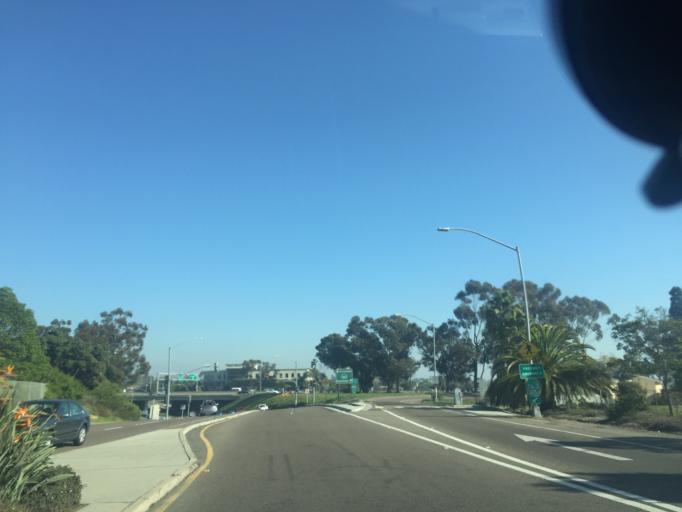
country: US
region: California
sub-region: San Diego County
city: San Diego
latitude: 32.7912
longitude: -117.1617
